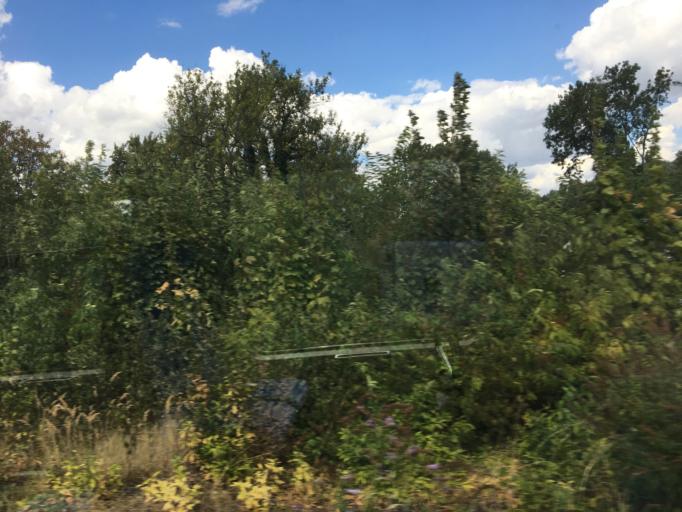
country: DE
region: North Rhine-Westphalia
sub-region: Regierungsbezirk Arnsberg
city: Bochum
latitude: 51.4806
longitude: 7.2894
